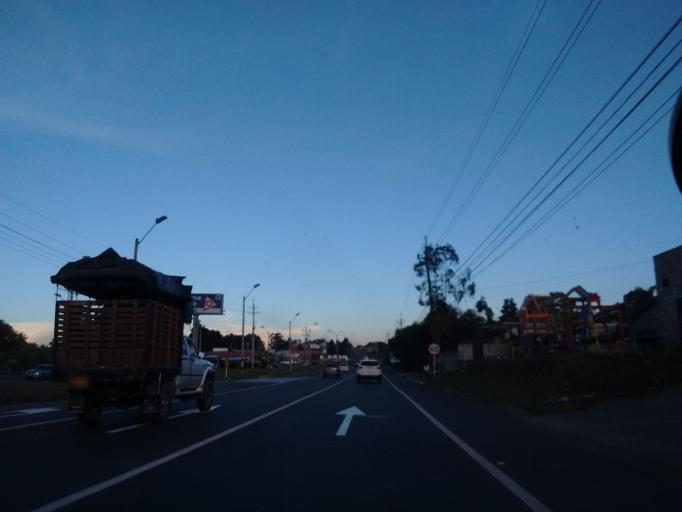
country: CO
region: Antioquia
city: Rionegro
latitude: 6.1856
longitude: -75.3770
